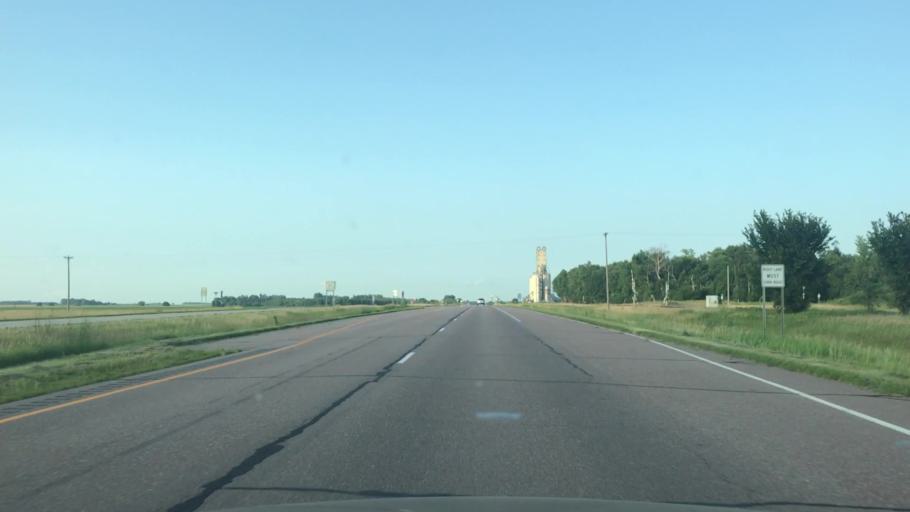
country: US
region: Minnesota
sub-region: Jackson County
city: Lakefield
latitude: 43.7627
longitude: -95.3727
